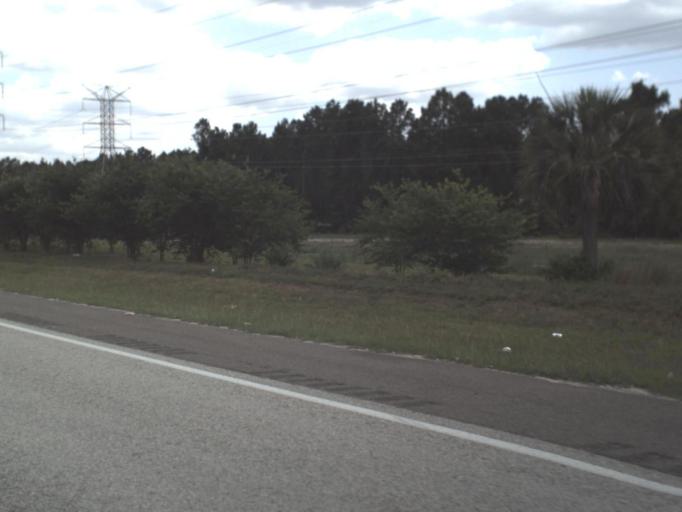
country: US
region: Florida
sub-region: Duval County
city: Jacksonville Beach
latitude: 30.2751
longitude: -81.5216
